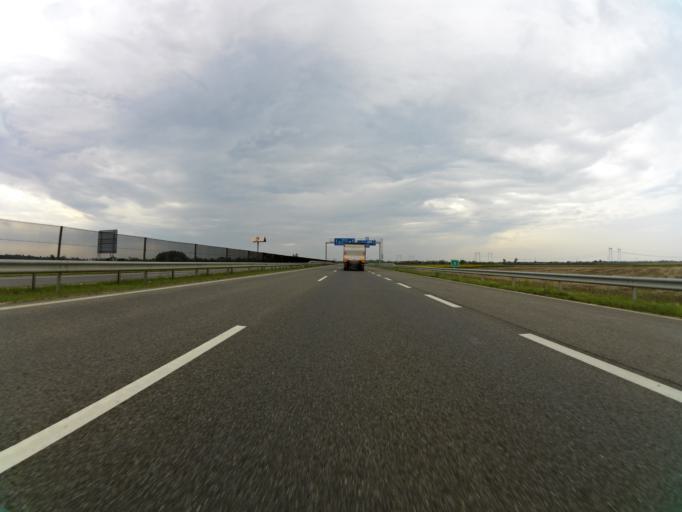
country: HU
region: Csongrad
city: Szeged
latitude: 46.2957
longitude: 20.1060
